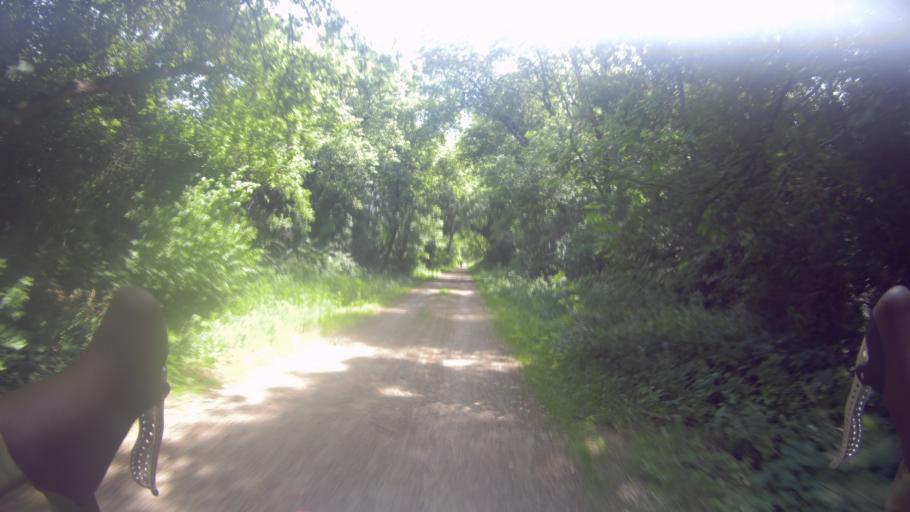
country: US
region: Wisconsin
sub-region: Jefferson County
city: Lake Mills
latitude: 43.0656
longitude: -88.9557
